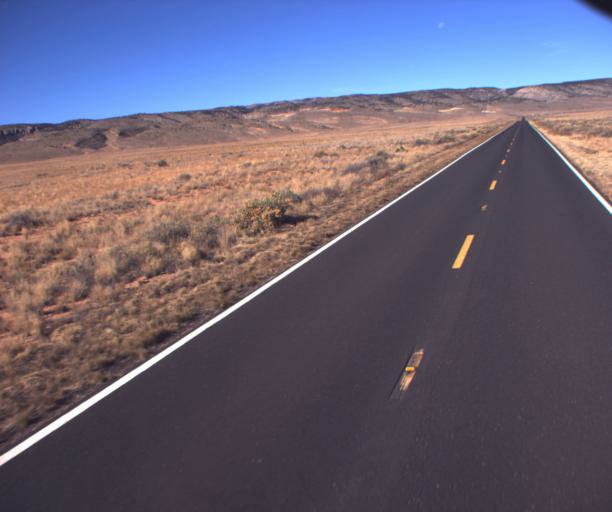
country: US
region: Arizona
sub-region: Coconino County
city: Fredonia
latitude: 36.7240
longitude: -112.0225
